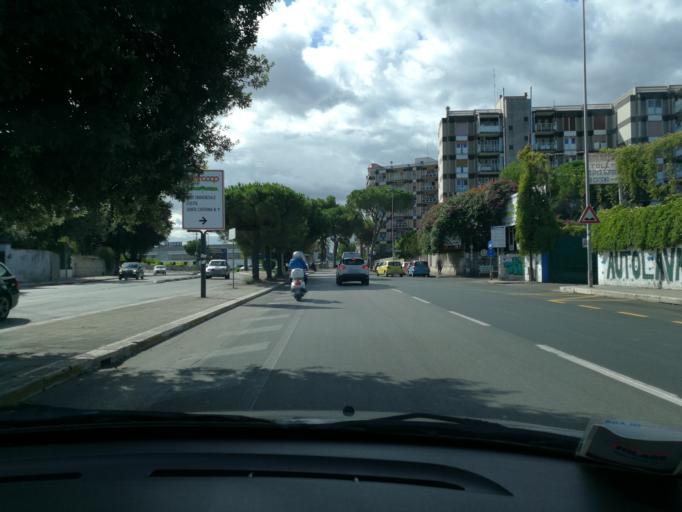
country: IT
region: Apulia
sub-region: Provincia di Bari
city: Bari
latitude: 41.1111
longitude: 16.8531
